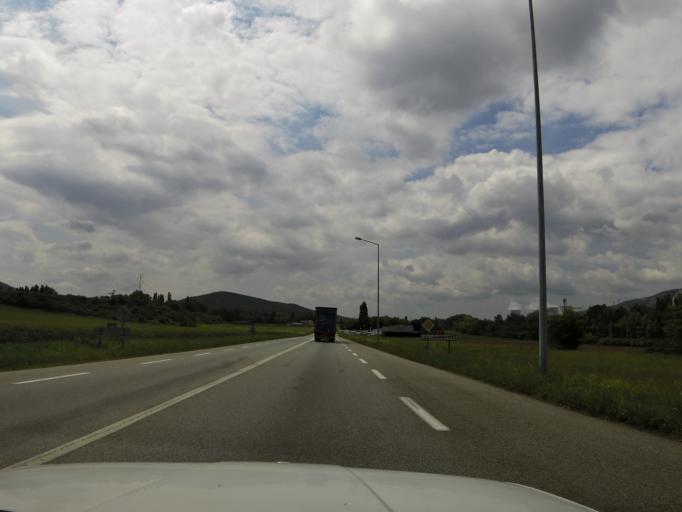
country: FR
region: Rhone-Alpes
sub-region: Departement de l'Ardeche
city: Cruas
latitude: 44.6600
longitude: 4.7890
